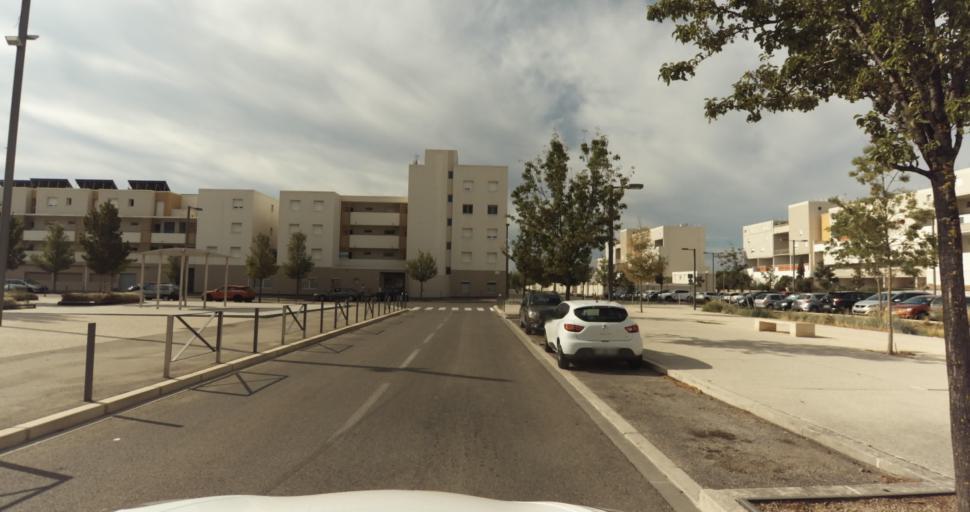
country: FR
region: Provence-Alpes-Cote d'Azur
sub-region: Departement des Bouches-du-Rhone
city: Miramas
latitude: 43.5975
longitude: 5.0085
